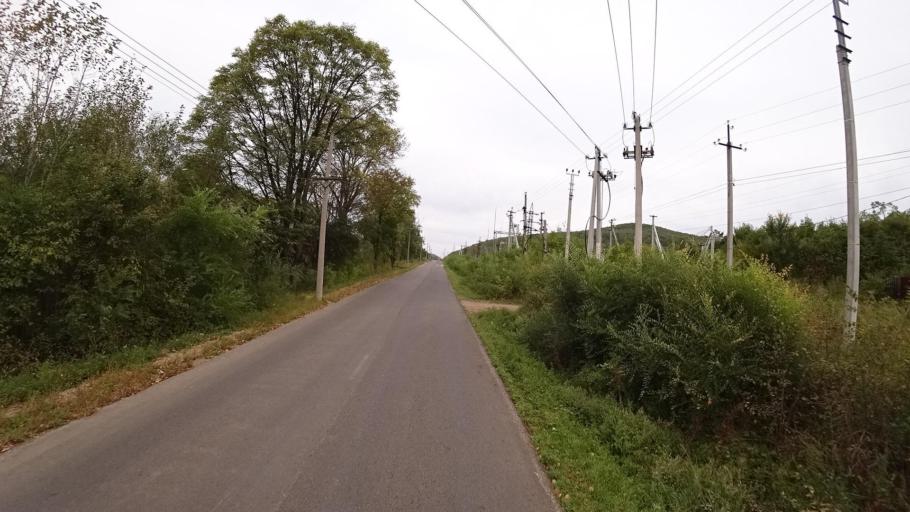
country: RU
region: Jewish Autonomous Oblast
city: Khingansk
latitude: 49.0353
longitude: 131.0588
